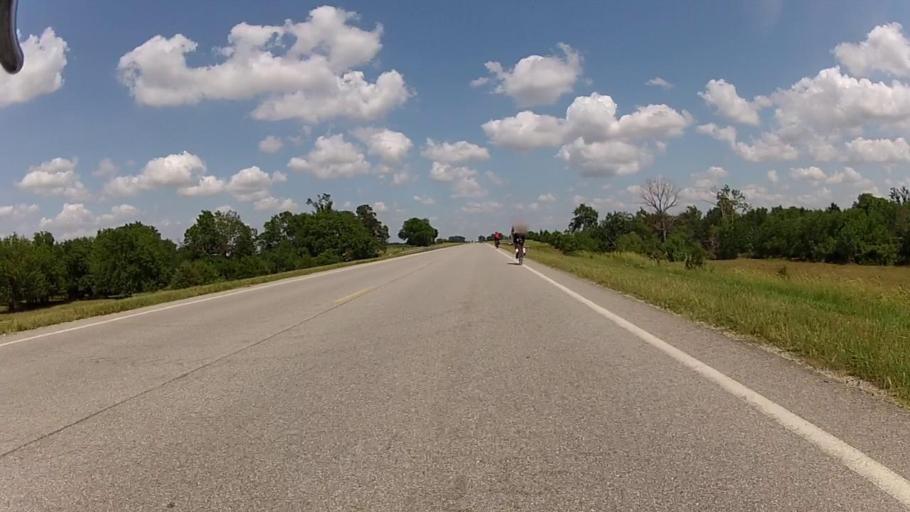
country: US
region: Kansas
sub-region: Labette County
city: Altamont
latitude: 37.1931
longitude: -95.2242
